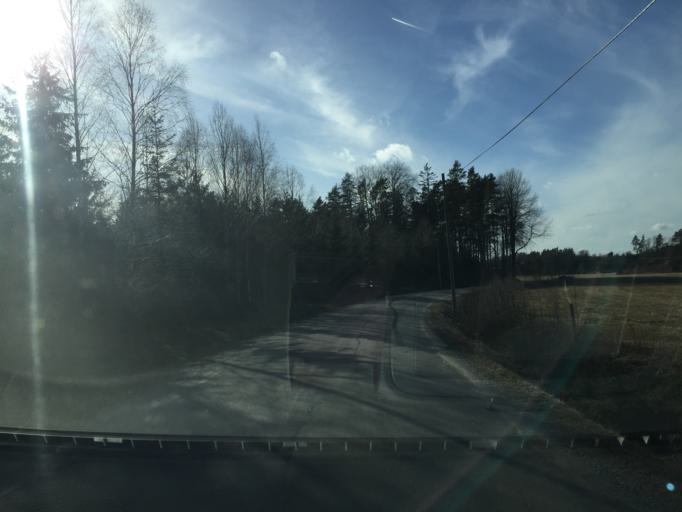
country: SE
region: Stockholm
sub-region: Nynashamns Kommun
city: Osmo
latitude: 59.0464
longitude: 17.8389
